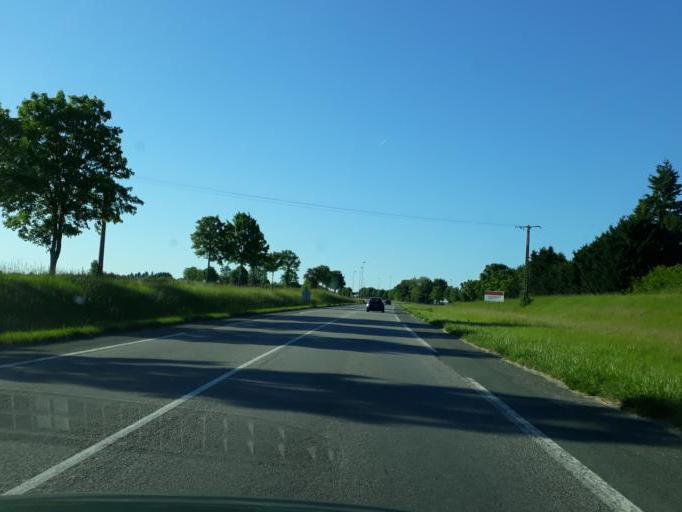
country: FR
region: Centre
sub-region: Departement du Loiret
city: Bonny-sur-Loire
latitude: 47.5645
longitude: 2.8329
